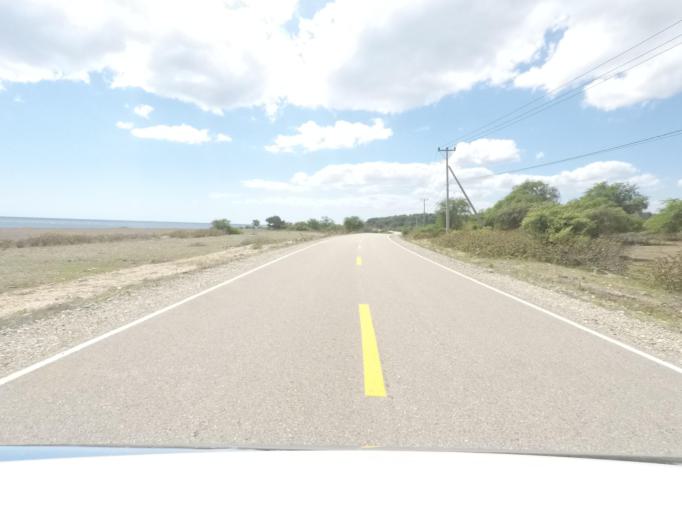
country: TL
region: Baucau
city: Baucau
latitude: -8.4136
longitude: 126.7154
